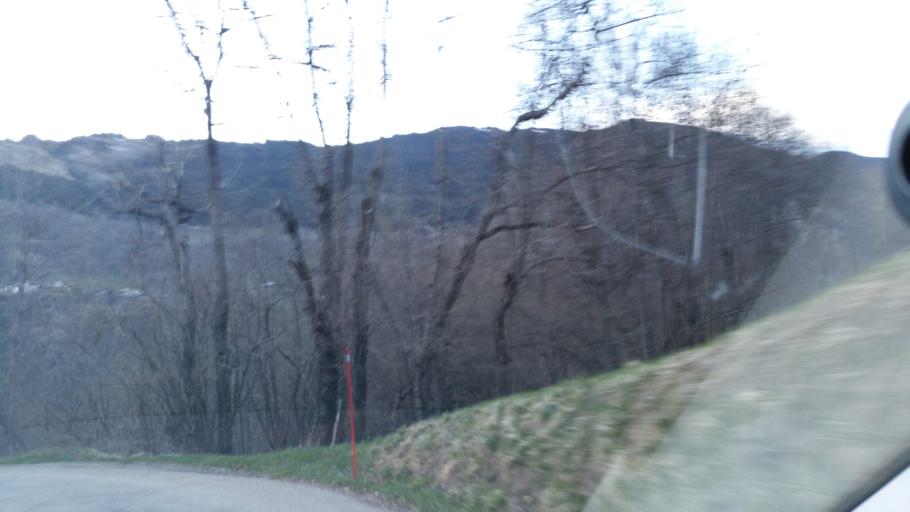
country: FR
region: Rhone-Alpes
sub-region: Departement de la Savoie
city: La Chambre
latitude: 45.3855
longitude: 6.3297
